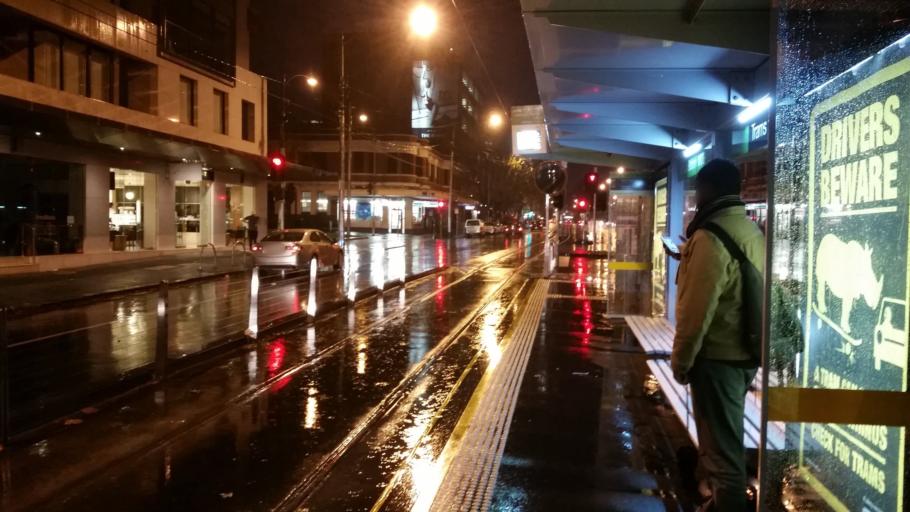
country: AU
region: Victoria
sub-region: Melbourne
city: East Melbourne
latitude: -37.8162
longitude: 144.9847
